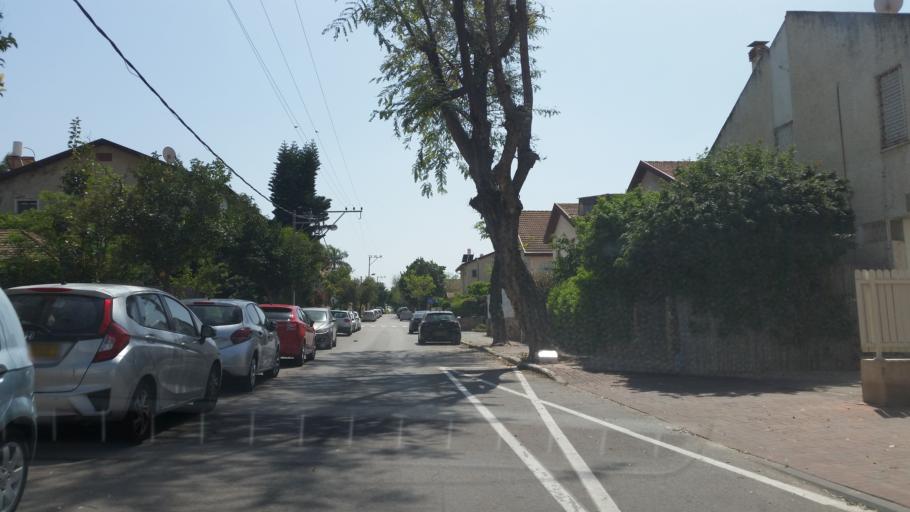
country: IL
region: Central District
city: Ra'anana
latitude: 32.1776
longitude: 34.8821
